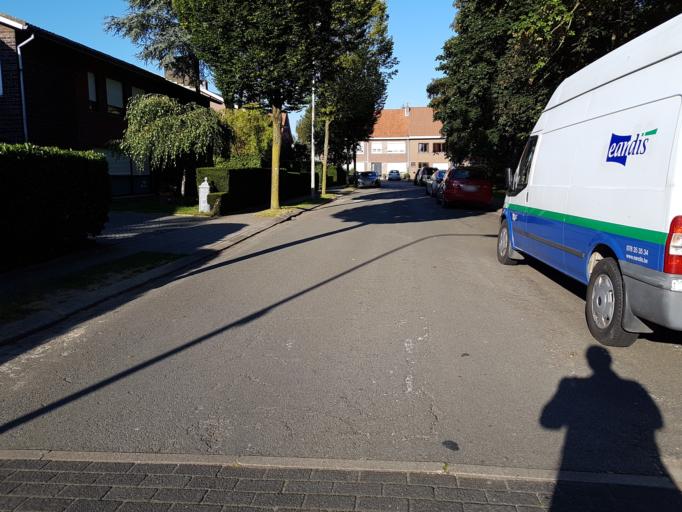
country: BE
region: Flanders
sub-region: Provincie Antwerpen
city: Hove
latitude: 51.1480
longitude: 4.4600
